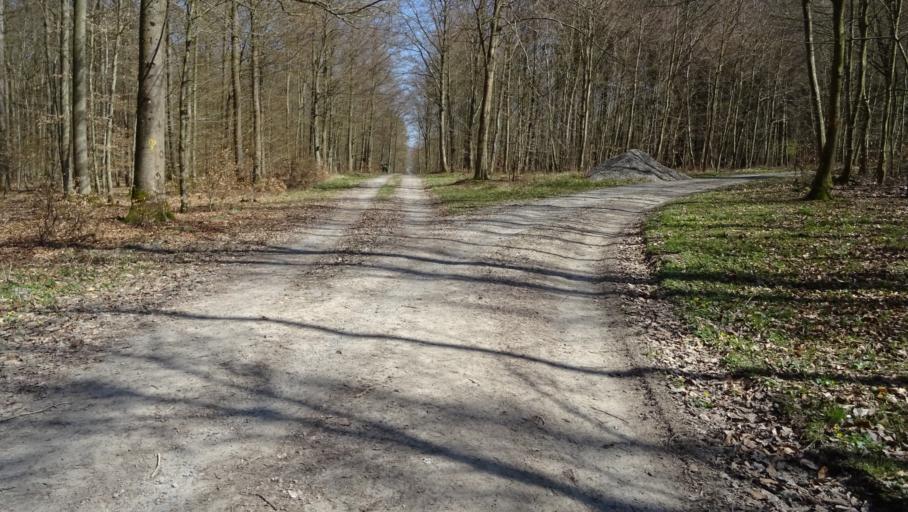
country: DE
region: Baden-Wuerttemberg
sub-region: Karlsruhe Region
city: Seckach
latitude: 49.4023
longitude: 9.3181
